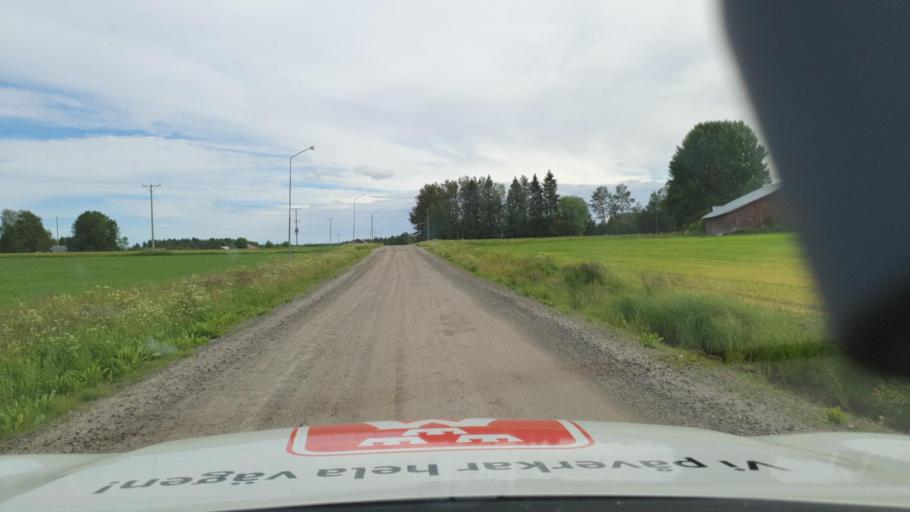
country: SE
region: Vaesterbotten
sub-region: Skelleftea Kommun
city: Burea
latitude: 64.3617
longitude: 21.0868
